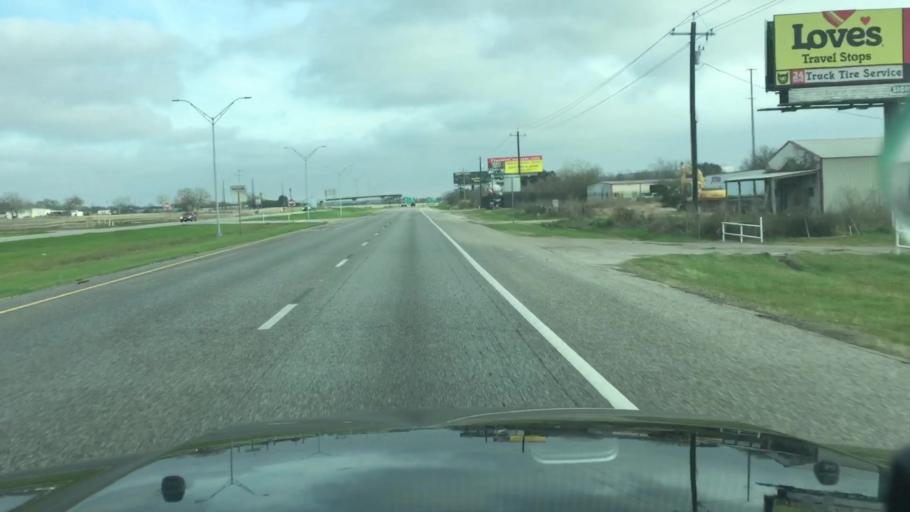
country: US
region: Texas
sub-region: Waller County
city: Hempstead
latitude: 30.1171
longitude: -96.0878
